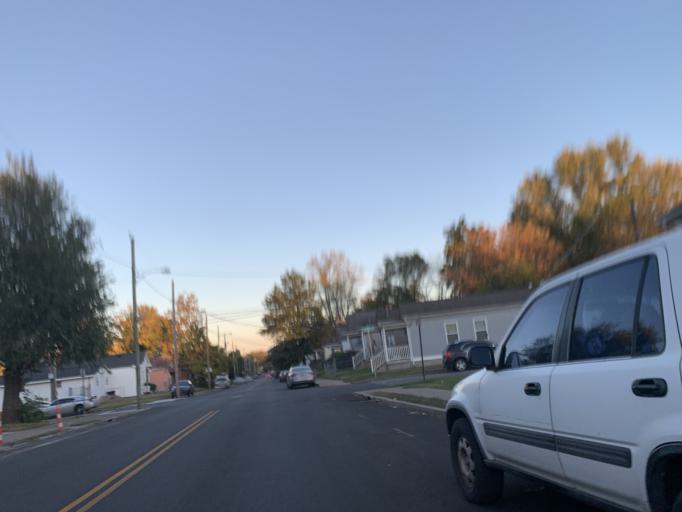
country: US
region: Kentucky
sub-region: Jefferson County
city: Louisville
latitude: 38.2351
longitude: -85.7933
